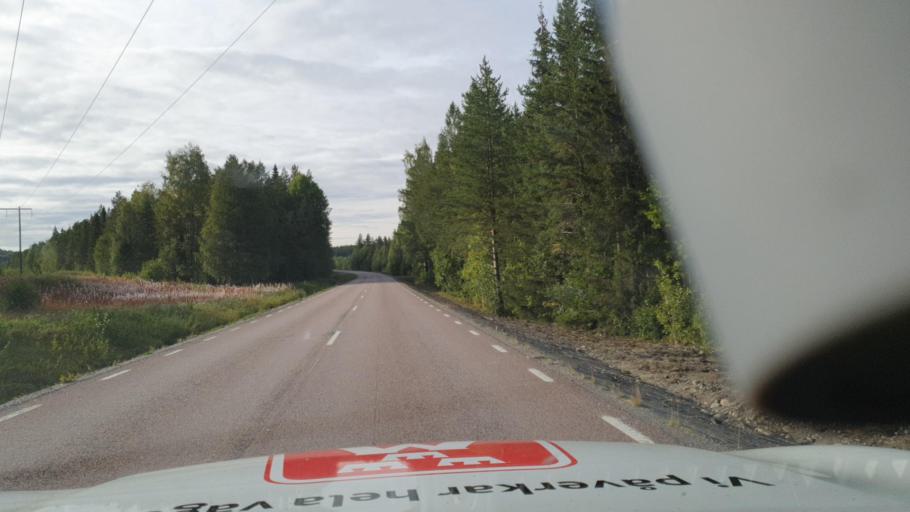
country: SE
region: Jaemtland
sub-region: Stroemsunds Kommun
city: Stroemsund
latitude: 63.7315
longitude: 15.7724
